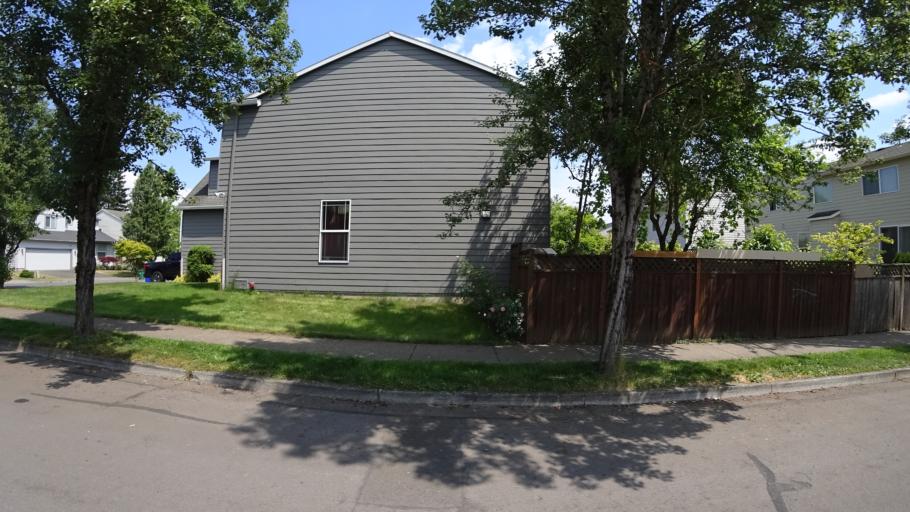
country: US
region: Oregon
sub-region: Multnomah County
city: Fairview
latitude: 45.5295
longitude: -122.4933
